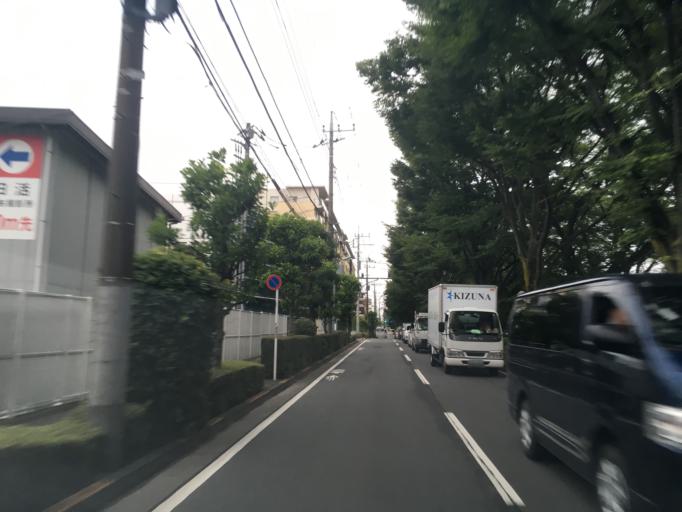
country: JP
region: Tokyo
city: Chofugaoka
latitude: 35.6392
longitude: 139.5508
